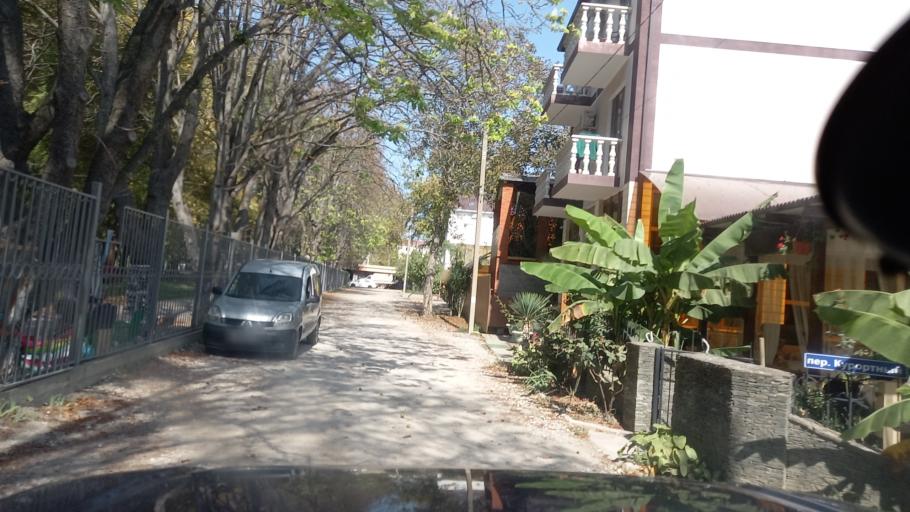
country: RU
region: Krasnodarskiy
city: Arkhipo-Osipovka
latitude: 44.3641
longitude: 38.5234
